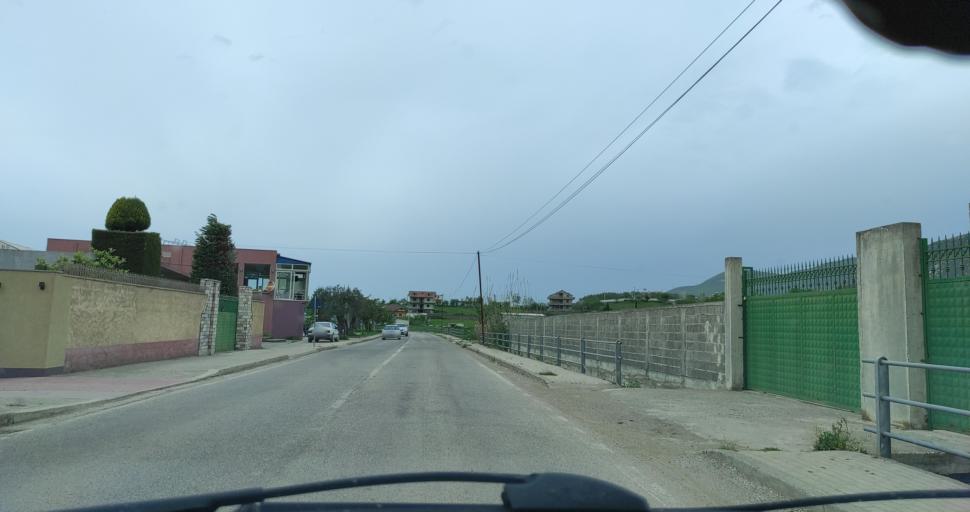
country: AL
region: Lezhe
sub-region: Rrethi i Kurbinit
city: Lac
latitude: 41.6096
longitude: 19.7135
